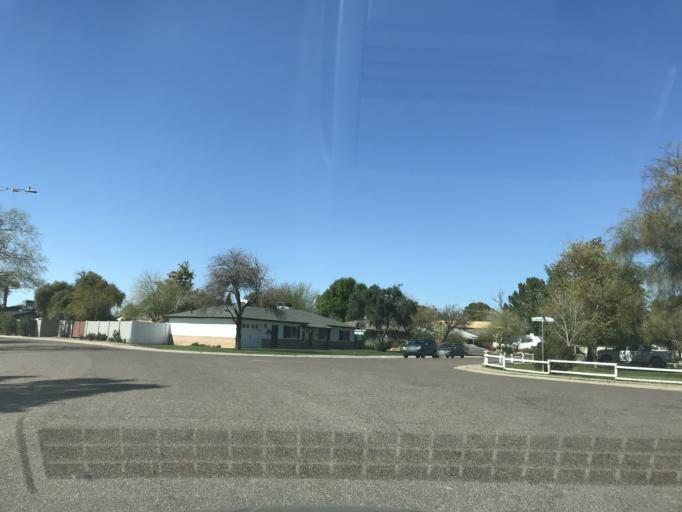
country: US
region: Arizona
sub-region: Maricopa County
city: Phoenix
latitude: 33.5190
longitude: -112.0883
